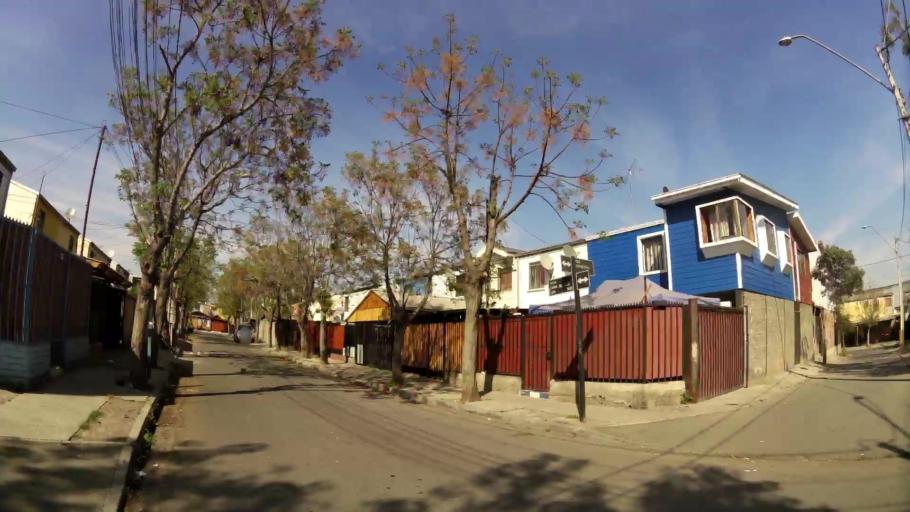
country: CL
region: Santiago Metropolitan
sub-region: Provincia de Santiago
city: La Pintana
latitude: -33.5641
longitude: -70.6346
